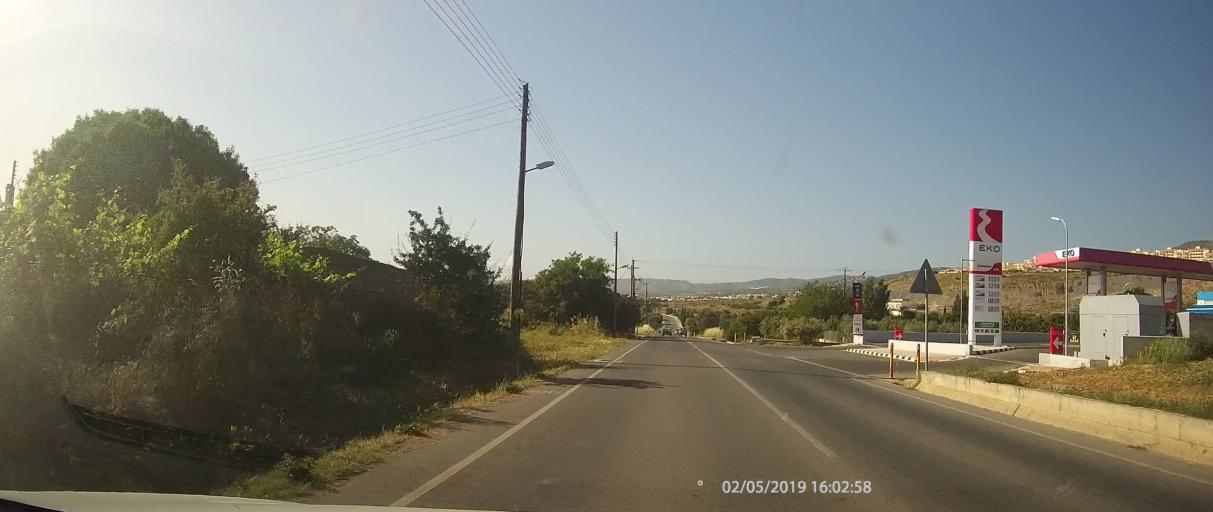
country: CY
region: Pafos
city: Empa
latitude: 34.8113
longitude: 32.4300
